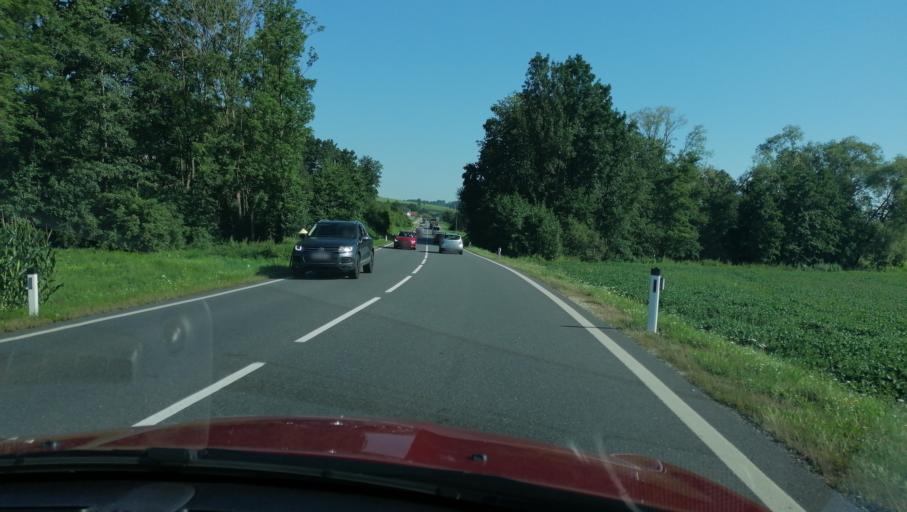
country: AT
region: Upper Austria
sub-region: Politischer Bezirk Grieskirchen
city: Bad Schallerbach
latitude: 48.2434
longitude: 13.9680
